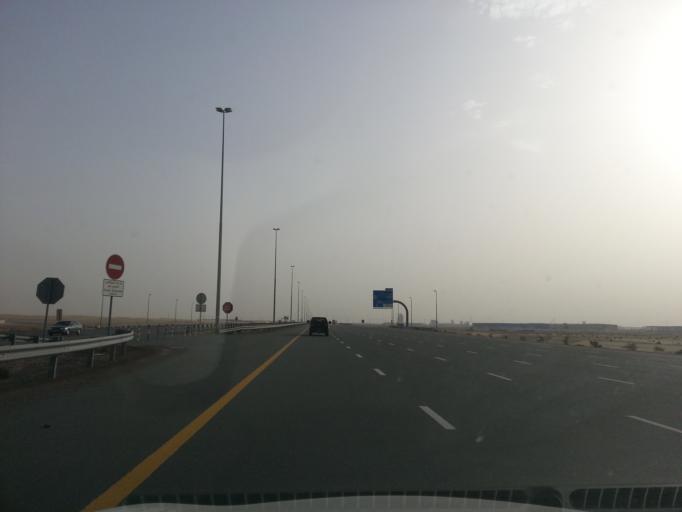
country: AE
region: Dubai
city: Dubai
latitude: 24.8163
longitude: 55.1136
